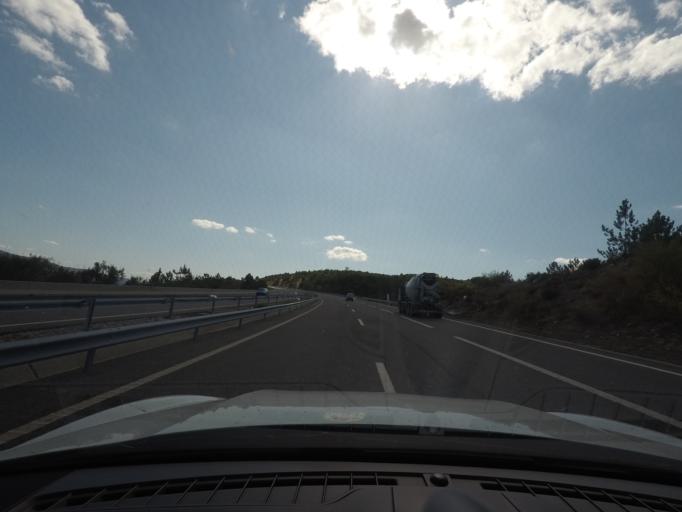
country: PT
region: Vila Real
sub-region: Vila Pouca de Aguiar
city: Vila Pouca de Aguiar
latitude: 41.5278
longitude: -7.6408
